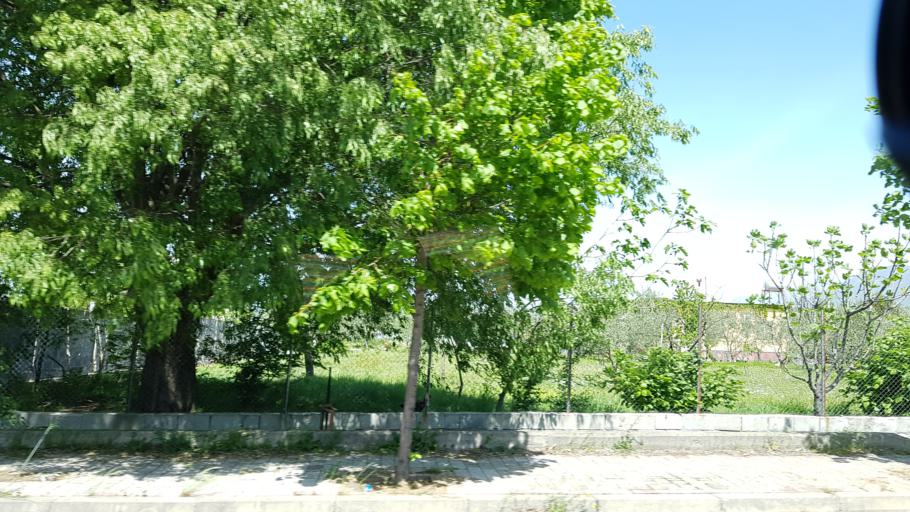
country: AL
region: Shkoder
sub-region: Rrethi i Shkodres
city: Shkoder
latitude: 42.1050
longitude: 19.5579
